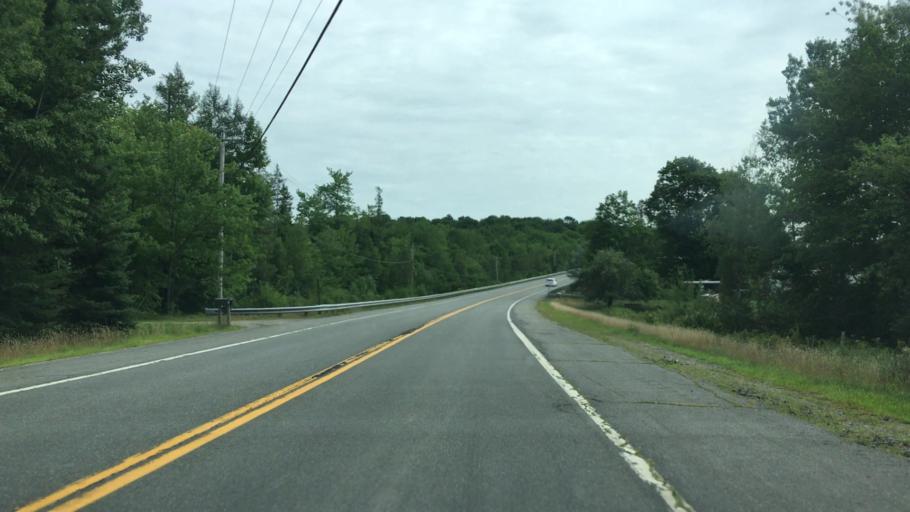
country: US
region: Maine
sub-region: Washington County
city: Calais
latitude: 45.0912
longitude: -67.4866
